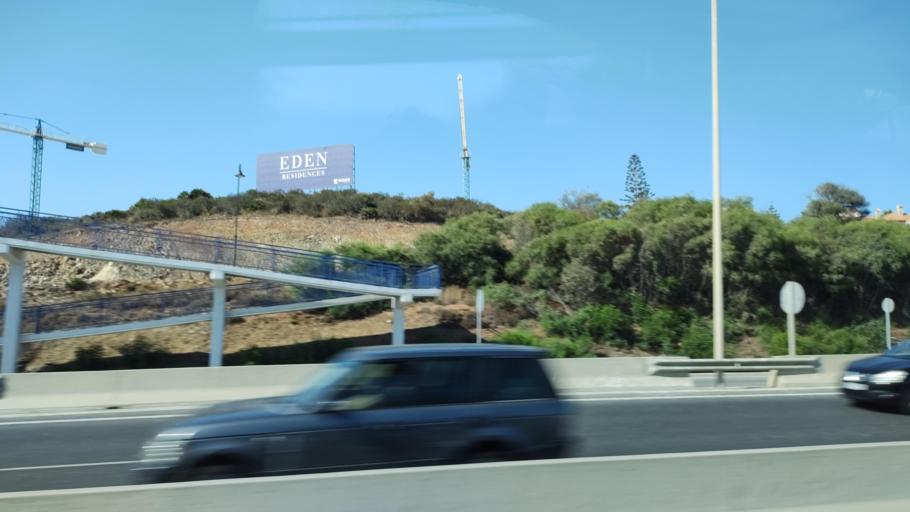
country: ES
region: Andalusia
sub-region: Provincia de Malaga
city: Fuengirola
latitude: 36.5069
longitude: -4.6571
